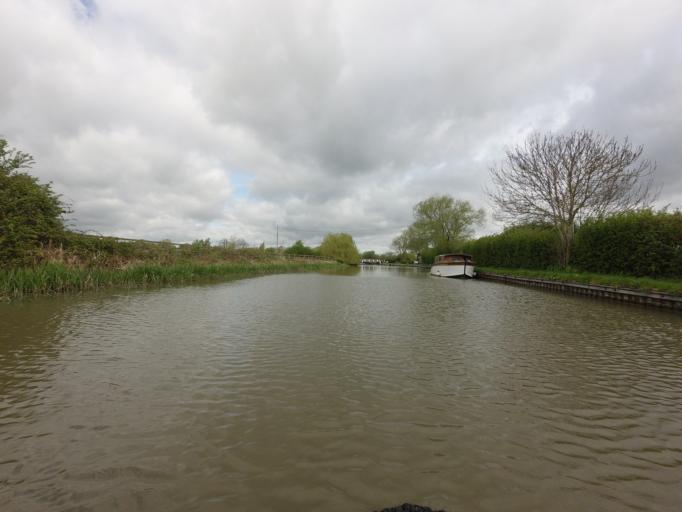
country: GB
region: England
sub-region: Milton Keynes
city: Water Eaton
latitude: 51.9604
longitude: -0.7102
